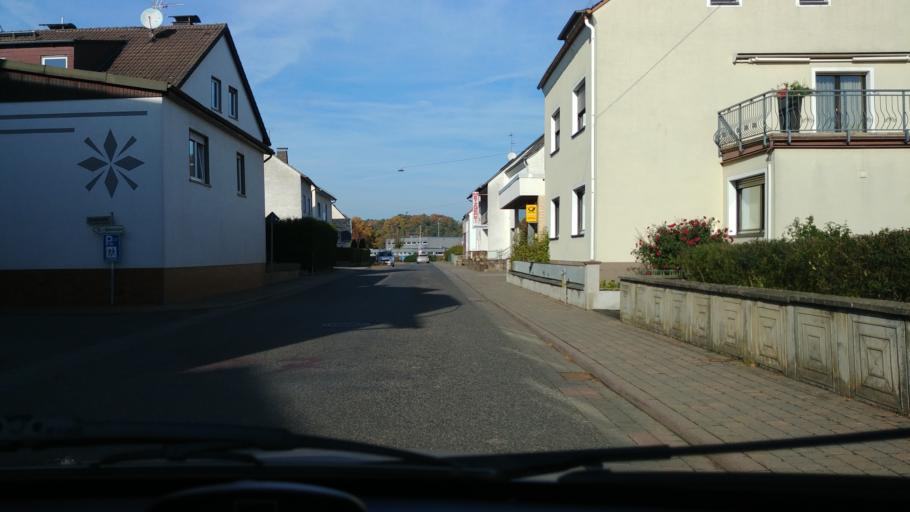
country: DE
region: Hesse
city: Burg Hohenstein
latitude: 50.2100
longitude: 8.0881
